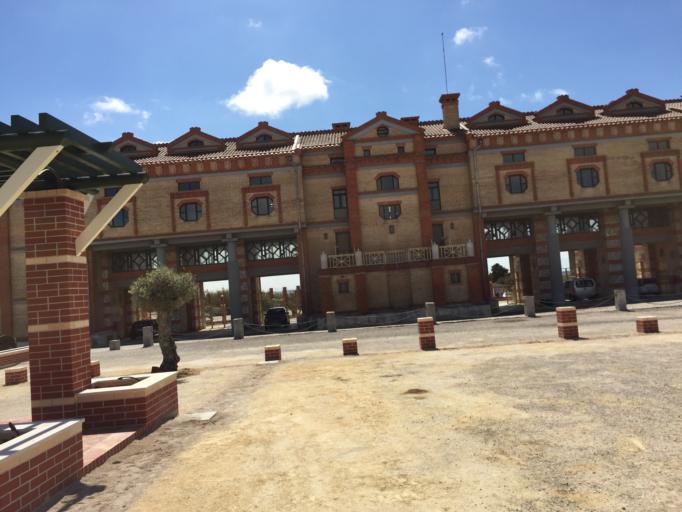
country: PT
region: Setubal
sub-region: Almada
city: Pragal
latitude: 38.6775
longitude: -9.1713
